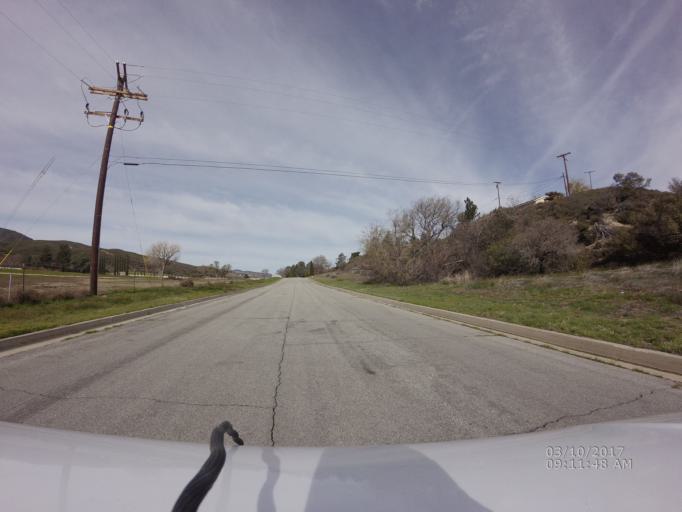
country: US
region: California
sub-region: Los Angeles County
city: Green Valley
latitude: 34.6549
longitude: -118.3858
